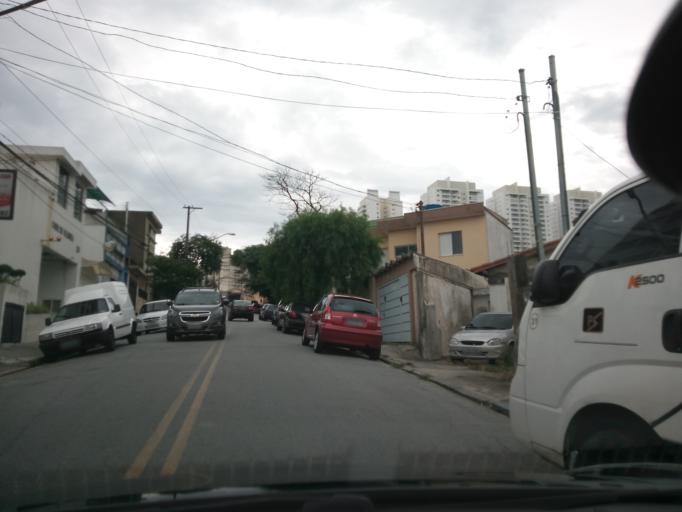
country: BR
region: Sao Paulo
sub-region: Sao Bernardo Do Campo
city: Sao Bernardo do Campo
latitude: -23.7132
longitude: -46.5577
